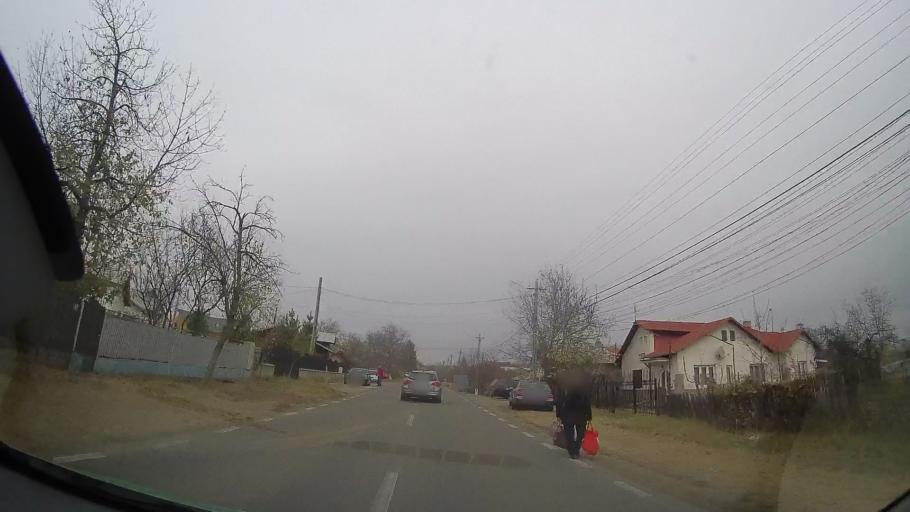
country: RO
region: Prahova
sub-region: Oras Baicoi
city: Liliesti
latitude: 45.0283
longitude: 25.8868
